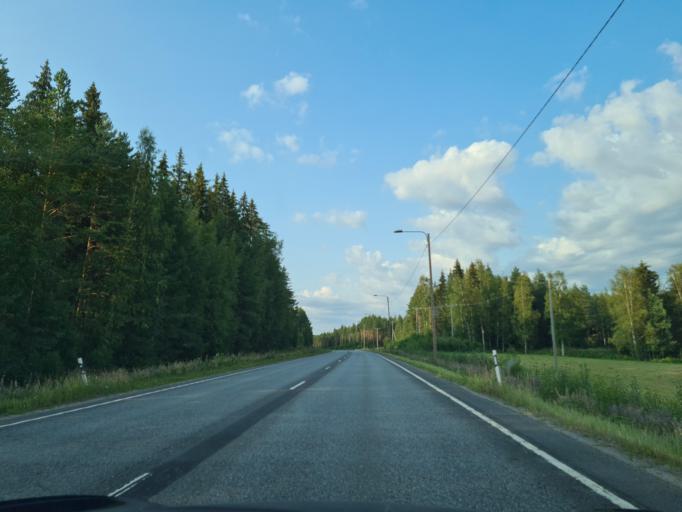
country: FI
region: Southern Ostrobothnia
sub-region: Seinaejoki
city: Kauhava
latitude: 63.0710
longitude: 23.0507
